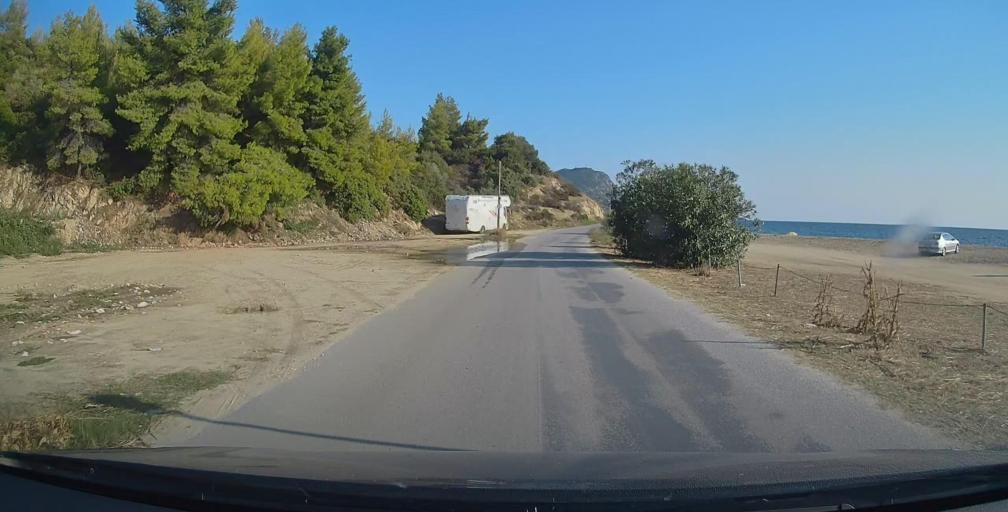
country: GR
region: Central Macedonia
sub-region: Nomos Chalkidikis
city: Sykia
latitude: 39.9915
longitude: 23.8934
